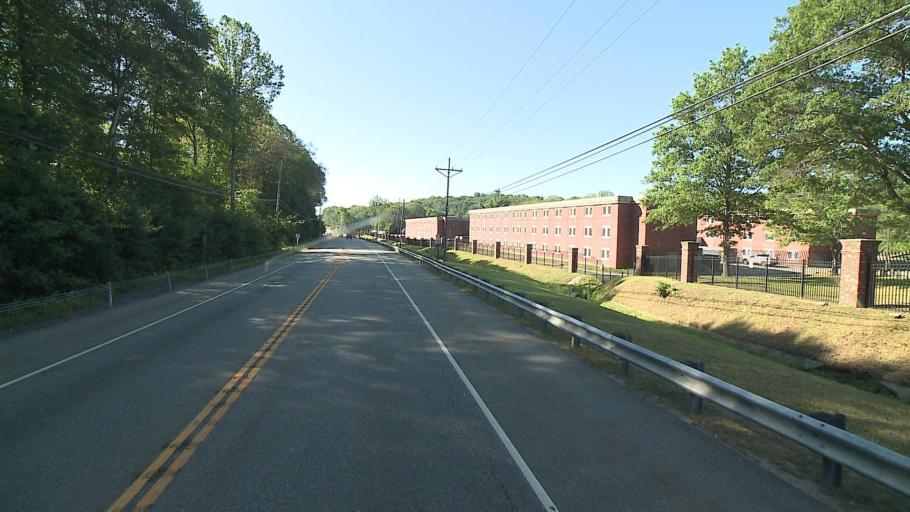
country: US
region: Connecticut
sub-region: New London County
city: Conning Towers-Nautilus Park
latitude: 41.3920
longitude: -72.0805
